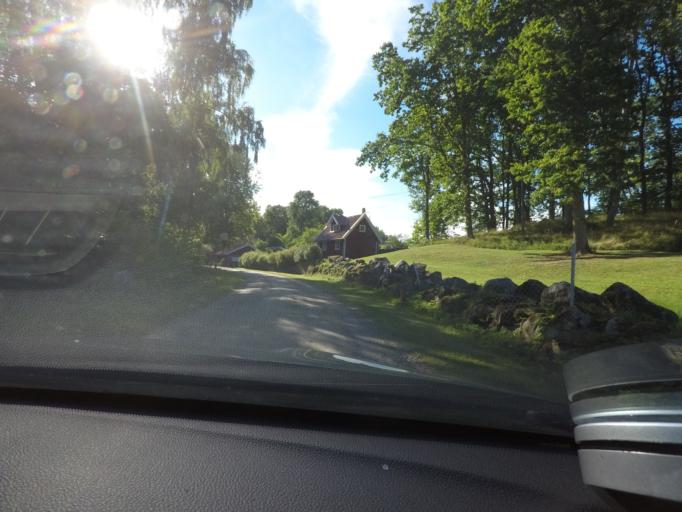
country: SE
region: Skane
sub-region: Hassleholms Kommun
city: Hassleholm
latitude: 56.1173
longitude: 13.8175
